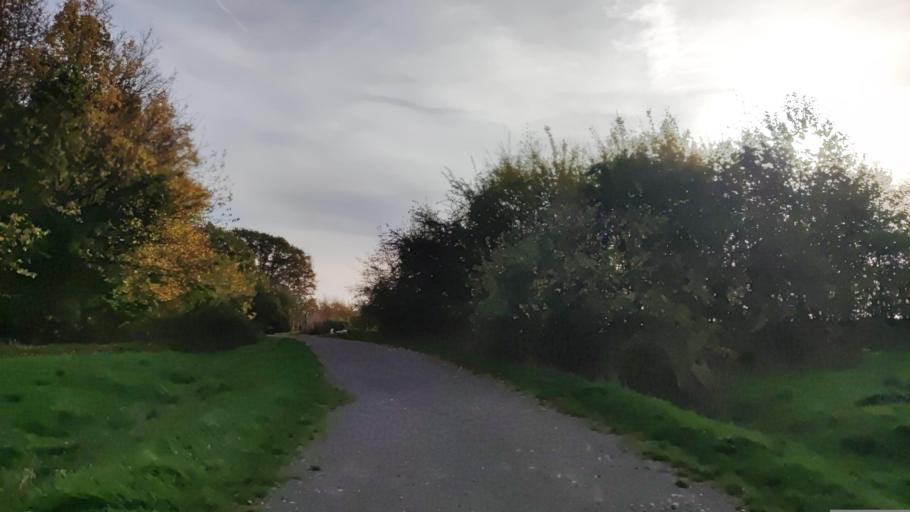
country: DE
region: North Rhine-Westphalia
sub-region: Regierungsbezirk Arnsberg
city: Herne
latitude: 51.5212
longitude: 7.2411
